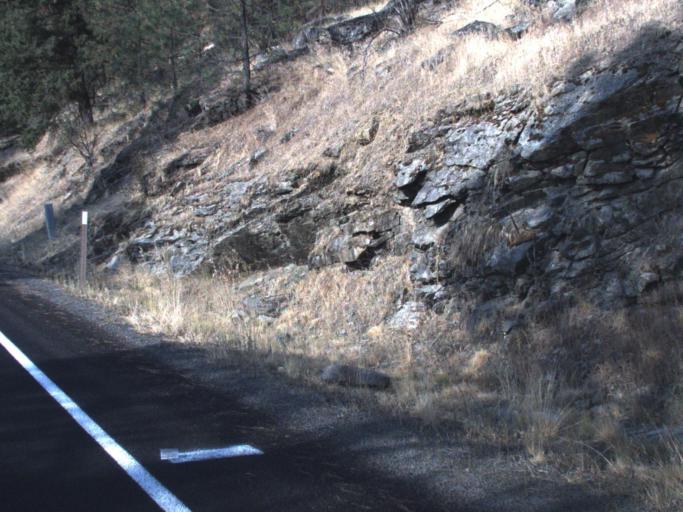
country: US
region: Washington
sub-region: Spokane County
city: Deer Park
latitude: 47.8881
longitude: -117.6907
